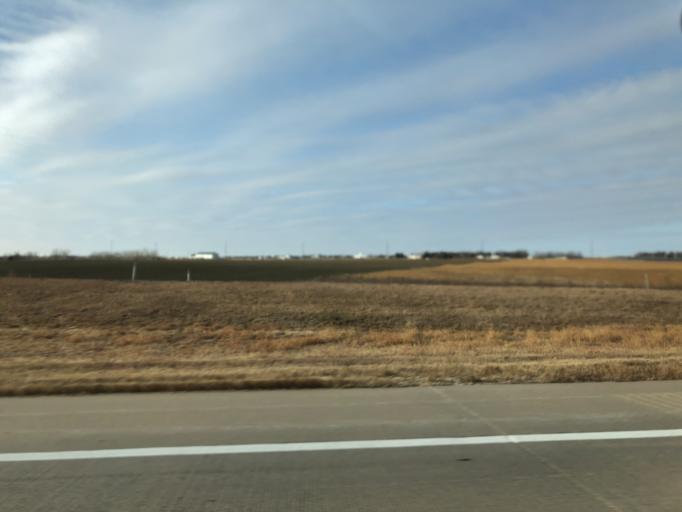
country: US
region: Kansas
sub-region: Reno County
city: South Hutchinson
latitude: 38.0181
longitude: -97.9687
